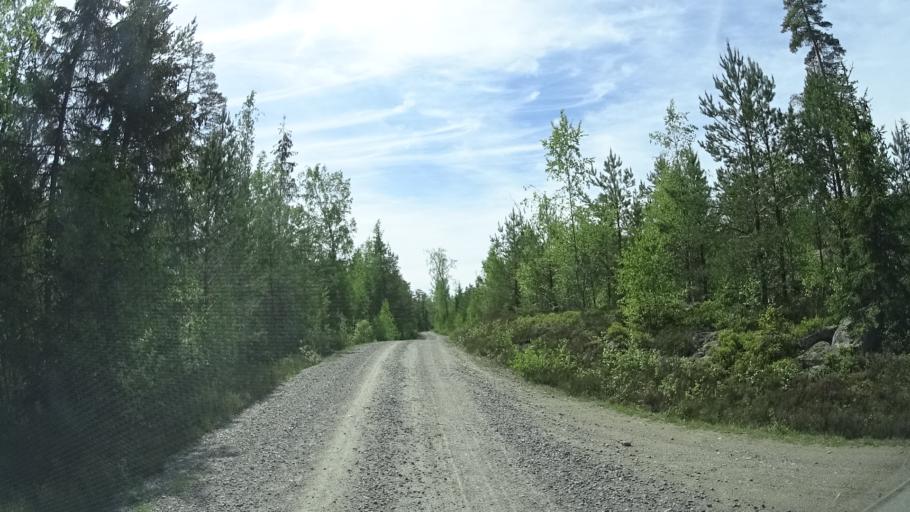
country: SE
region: OEstergoetland
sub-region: Finspangs Kommun
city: Finspang
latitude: 58.7822
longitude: 15.8468
